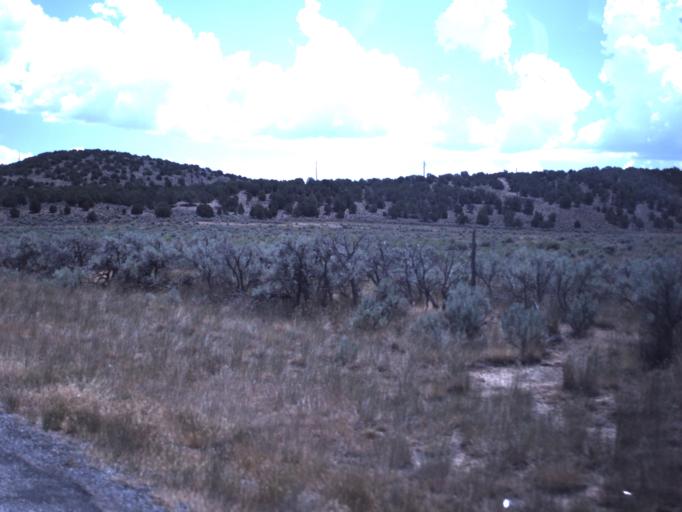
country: US
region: Utah
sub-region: Juab County
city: Nephi
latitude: 39.6976
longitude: -111.9594
